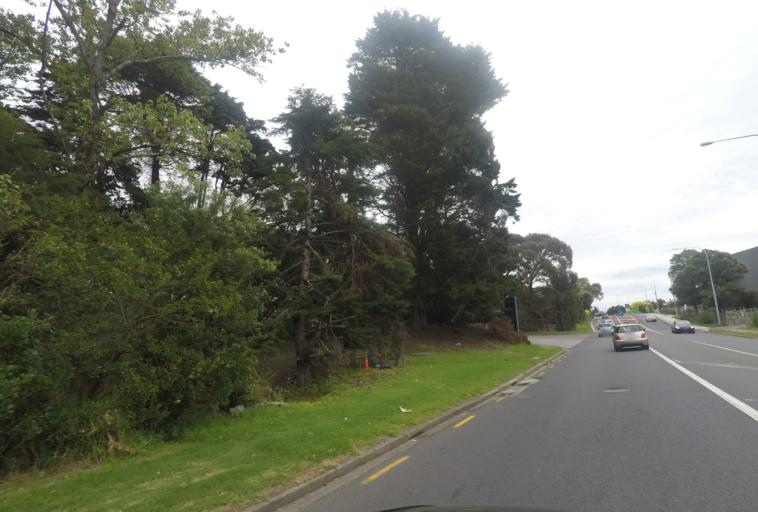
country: NZ
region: Auckland
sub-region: Auckland
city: Mangere
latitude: -36.9485
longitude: 174.8284
